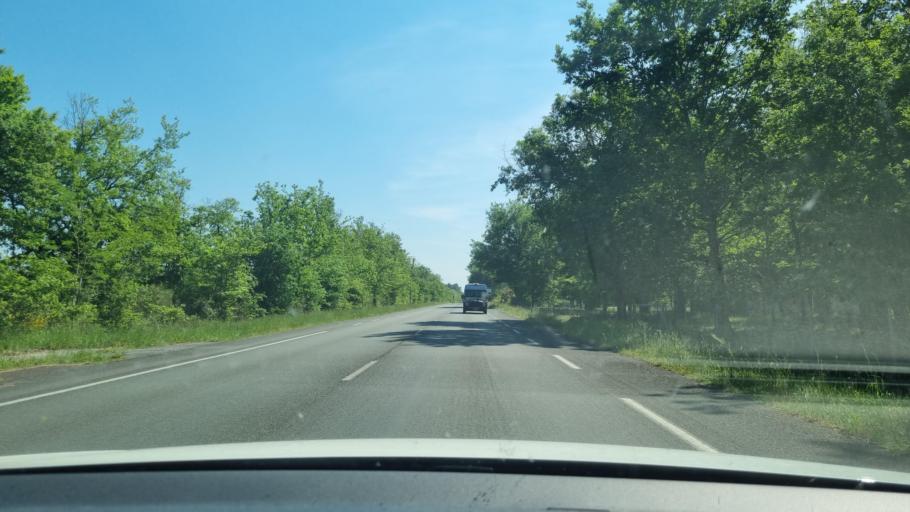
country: FR
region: Aquitaine
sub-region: Departement des Landes
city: Roquefort
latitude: 44.2065
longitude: -0.2684
